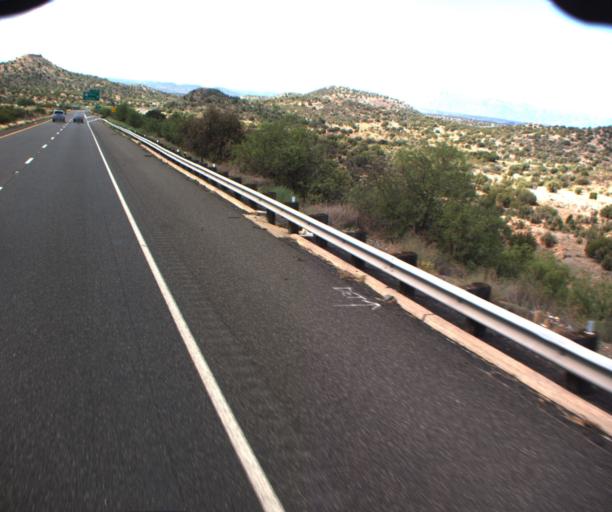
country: US
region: Arizona
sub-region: Yavapai County
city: Lake Montezuma
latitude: 34.6957
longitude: -111.7441
